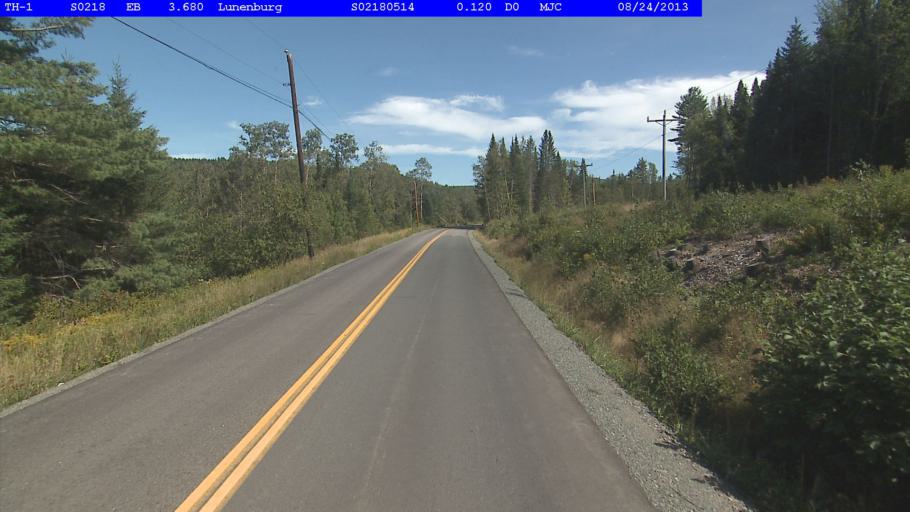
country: US
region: New Hampshire
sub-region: Grafton County
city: Littleton
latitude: 44.4201
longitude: -71.7452
